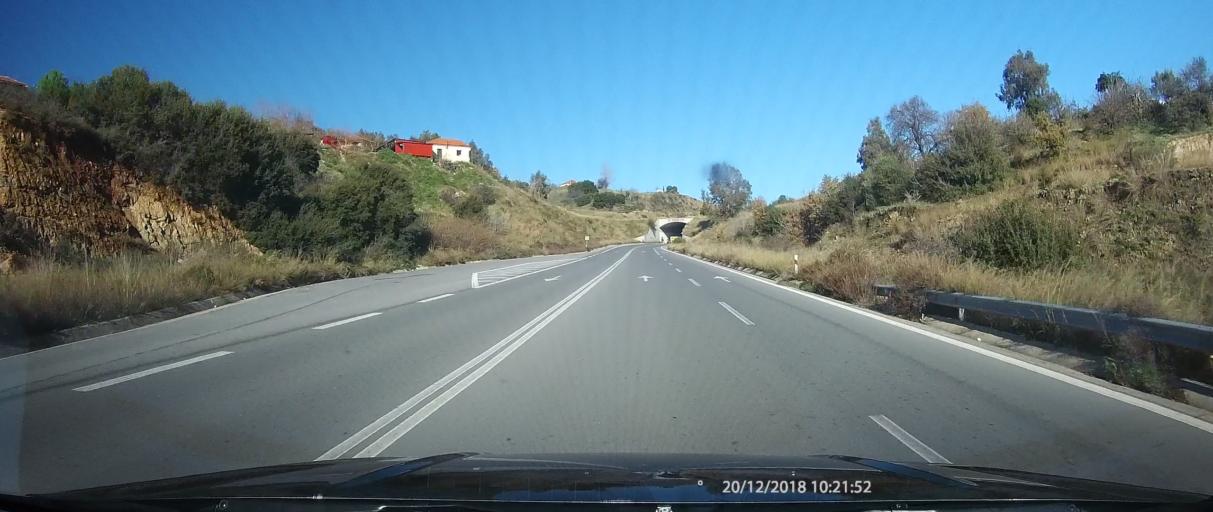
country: GR
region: Peloponnese
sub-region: Nomos Lakonias
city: Magoula
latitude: 37.1665
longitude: 22.4265
